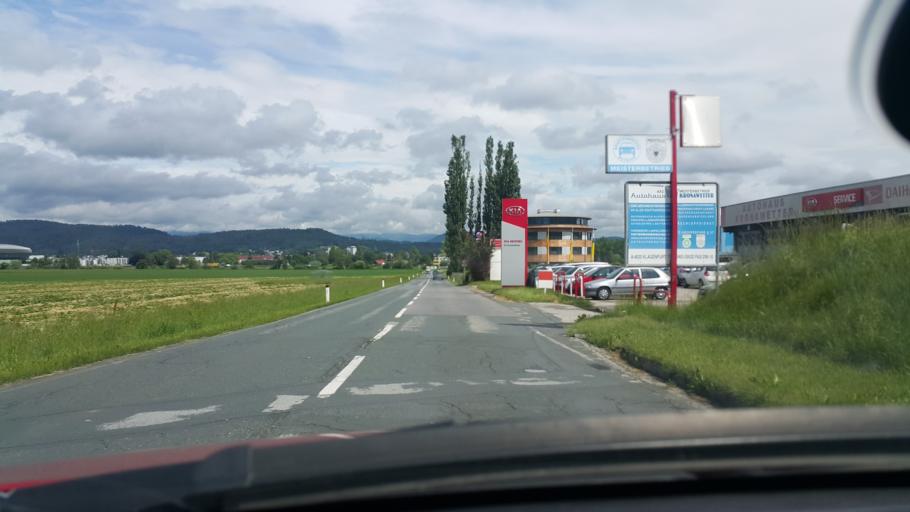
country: AT
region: Carinthia
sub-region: Klagenfurt am Woerthersee
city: Klagenfurt am Woerthersee
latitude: 46.5980
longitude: 14.2902
